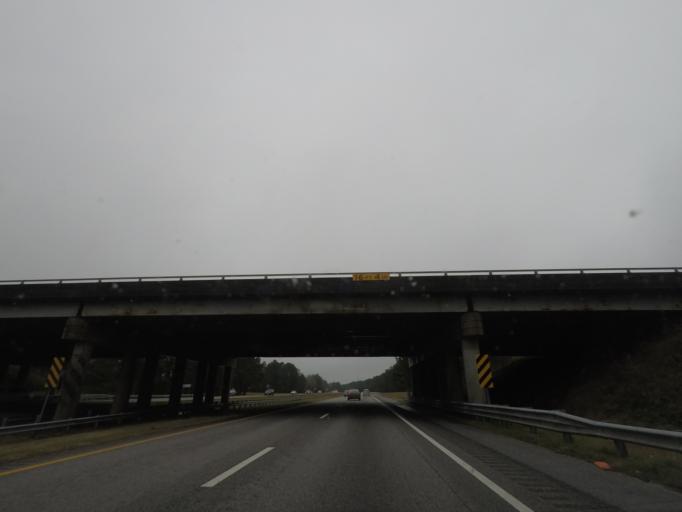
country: US
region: South Carolina
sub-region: Sumter County
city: East Sumter
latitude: 33.9016
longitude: -80.0931
